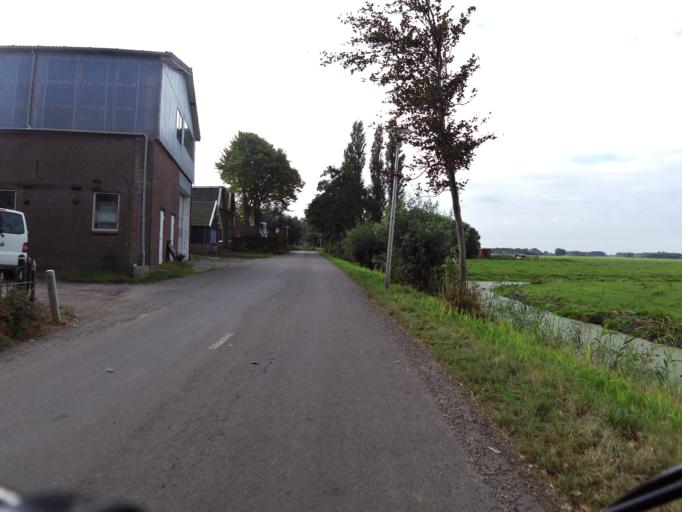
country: NL
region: South Holland
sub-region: Gemeente Rijnwoude
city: Benthuizen
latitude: 52.1098
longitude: 4.5206
